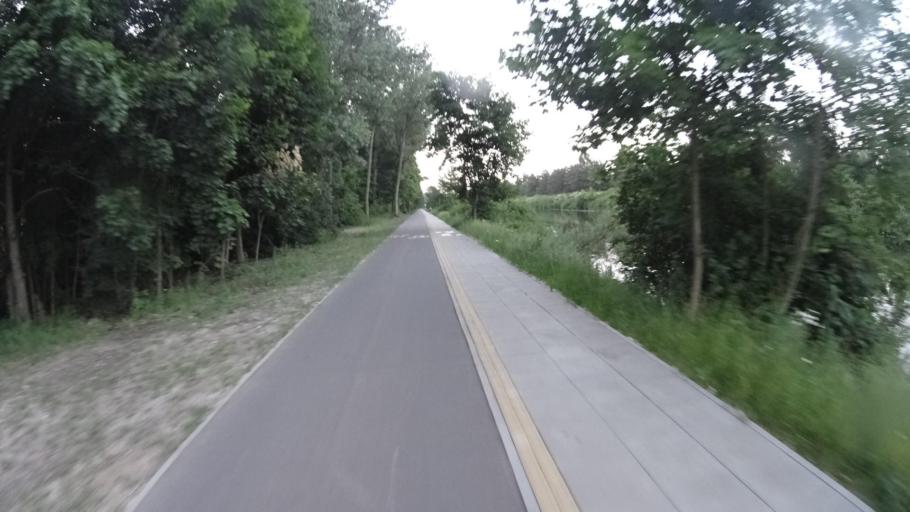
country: PL
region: Masovian Voivodeship
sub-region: Powiat legionowski
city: Stanislawow Pierwszy
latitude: 52.3832
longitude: 21.0359
